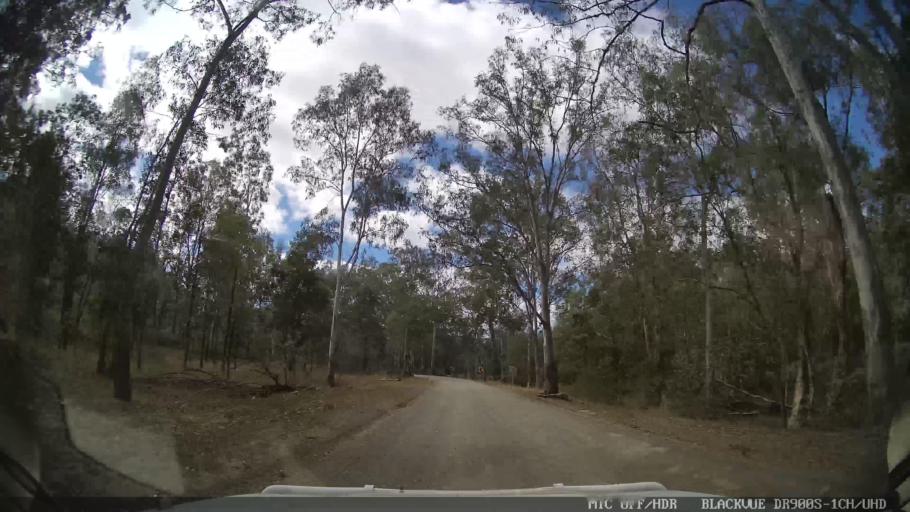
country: AU
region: Queensland
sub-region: Gladstone
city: Toolooa
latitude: -24.5509
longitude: 151.3401
